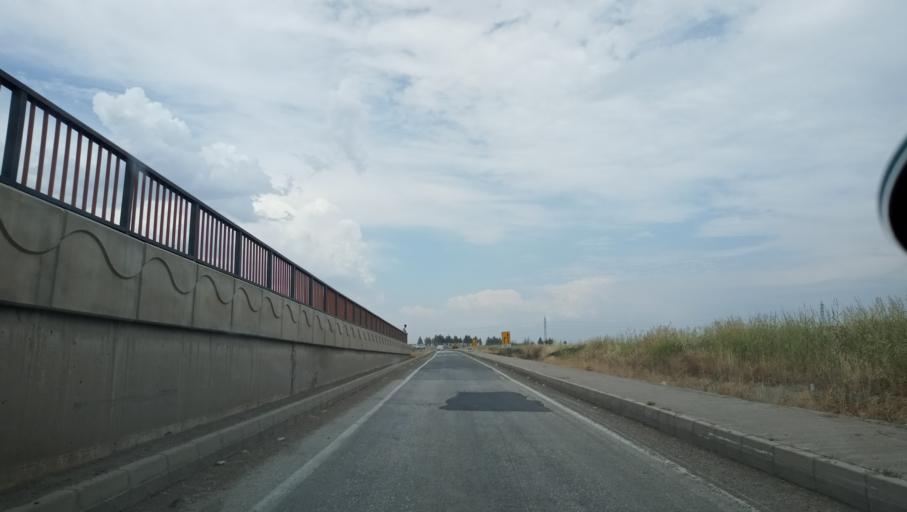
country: TR
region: Diyarbakir
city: Cinar
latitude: 37.8107
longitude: 40.3319
